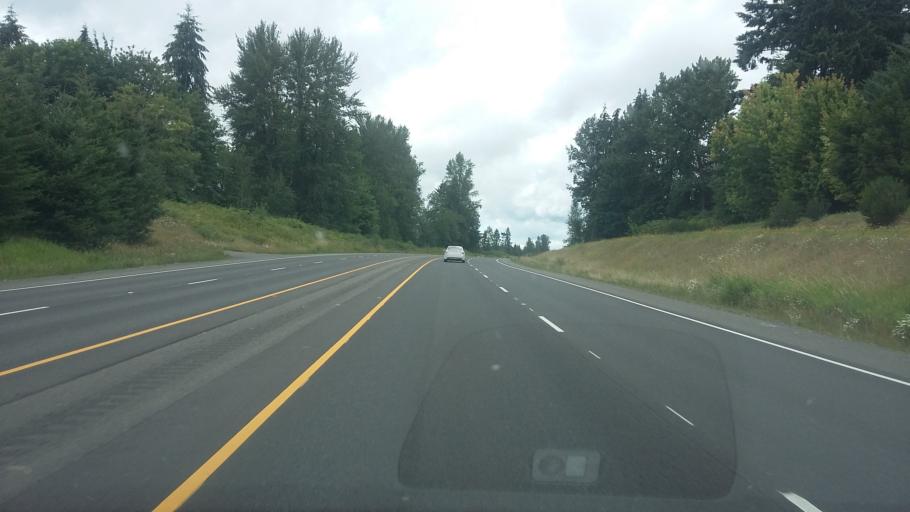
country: US
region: Washington
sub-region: Clark County
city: Brush Prairie
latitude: 45.7435
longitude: -122.5516
